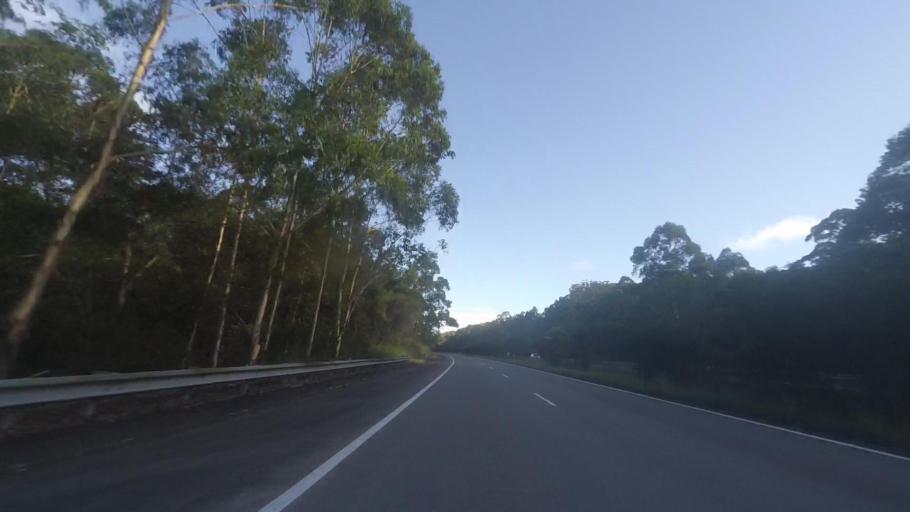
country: AU
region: New South Wales
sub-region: Great Lakes
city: Bulahdelah
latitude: -32.2757
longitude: 152.3296
